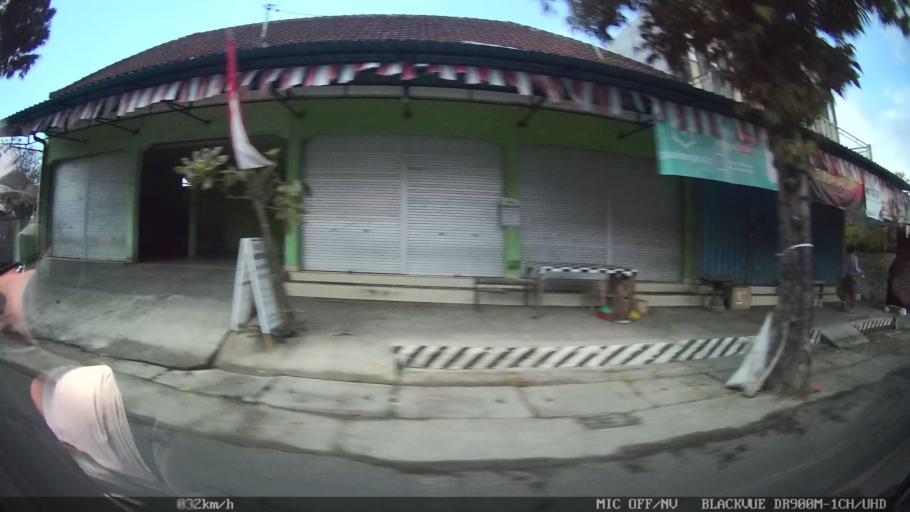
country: ID
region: Bali
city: Banjar Pasekan
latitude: -8.5990
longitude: 115.2880
